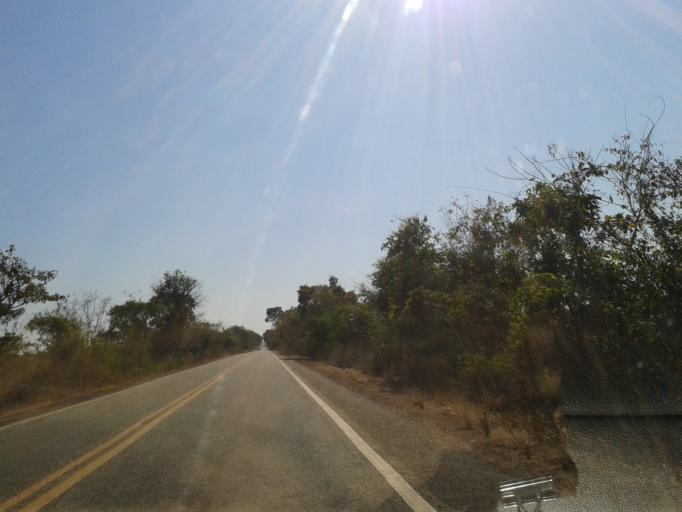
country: BR
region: Goias
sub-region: Mozarlandia
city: Mozarlandia
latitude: -14.4919
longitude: -50.4828
